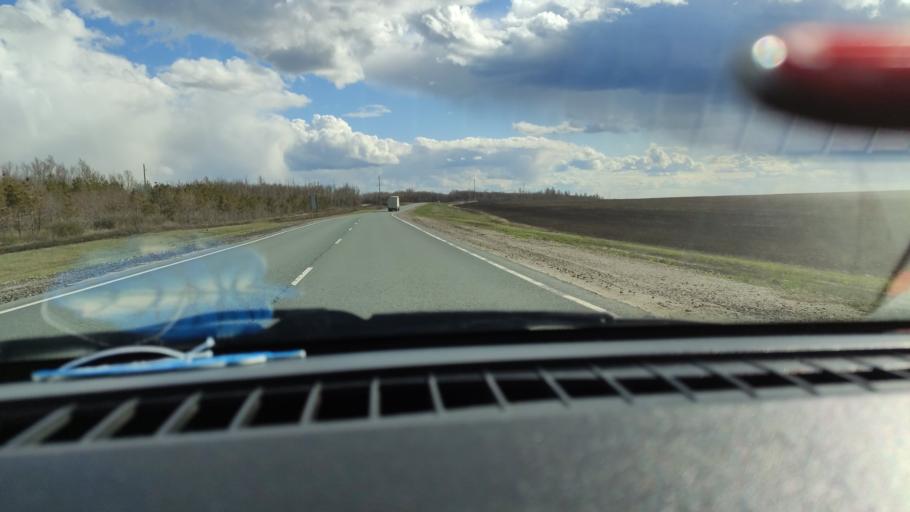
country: RU
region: Saratov
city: Alekseyevka
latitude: 52.2755
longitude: 47.9309
